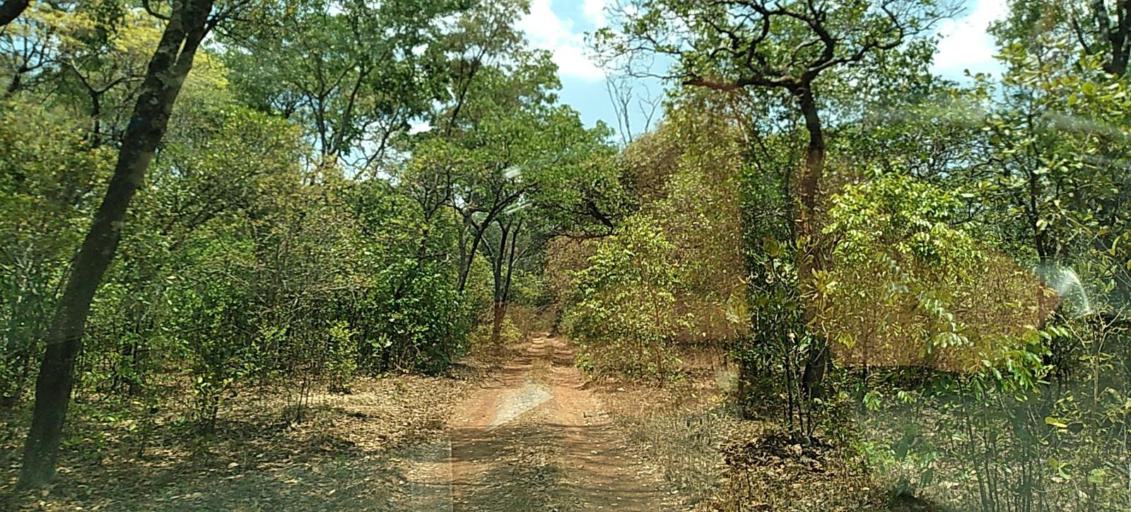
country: ZM
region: Copperbelt
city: Chililabombwe
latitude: -12.4711
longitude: 27.7001
